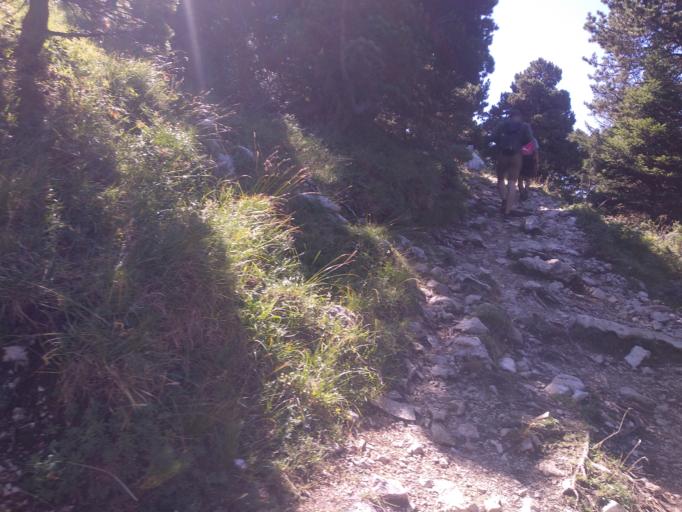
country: FR
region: Rhone-Alpes
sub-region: Departement de l'Isere
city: Le Sappey-en-Chartreuse
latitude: 45.2850
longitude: 5.7826
